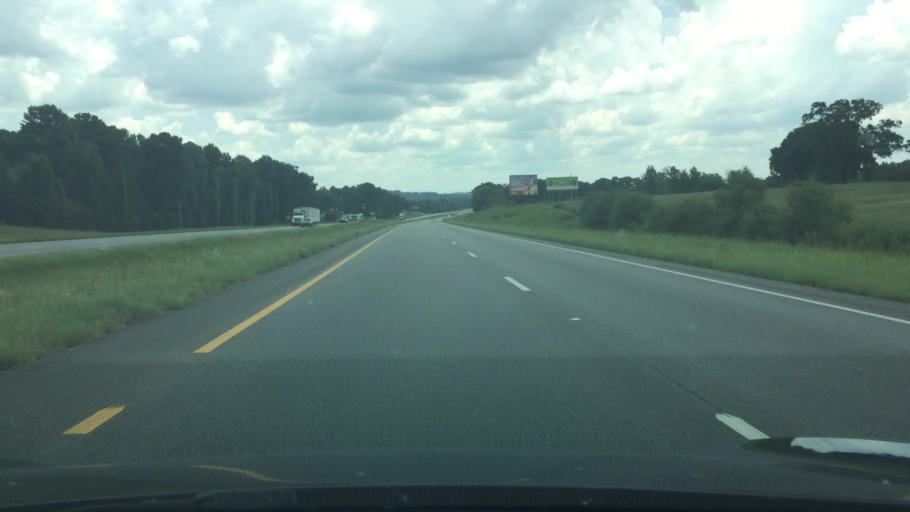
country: US
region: Alabama
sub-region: Pike County
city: Troy
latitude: 31.8752
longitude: -86.0028
